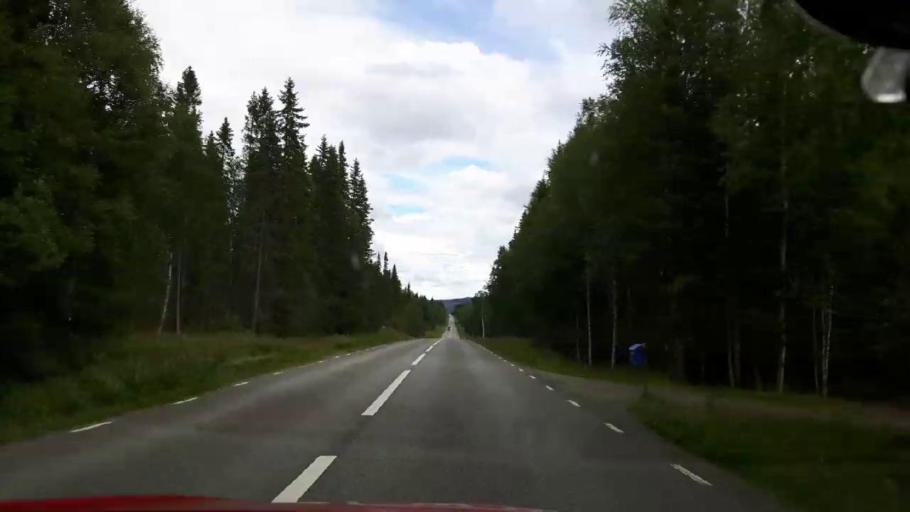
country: NO
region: Nord-Trondelag
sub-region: Lierne
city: Sandvika
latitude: 64.3899
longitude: 14.4253
